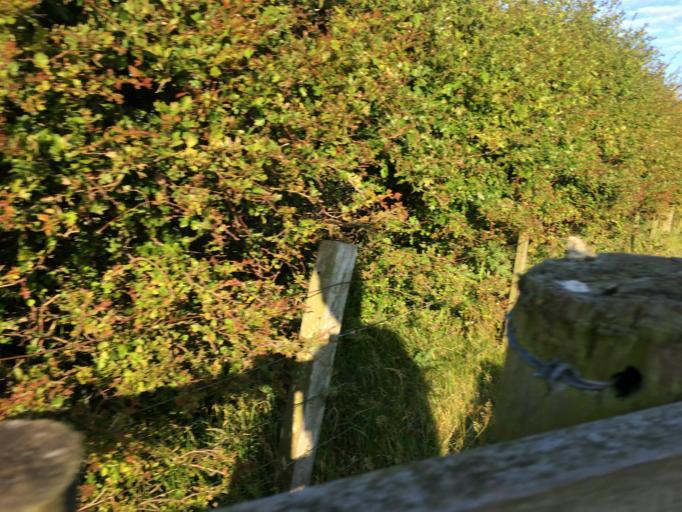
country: GB
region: England
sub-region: Northumberland
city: Bamburgh
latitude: 55.5988
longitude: -1.6963
